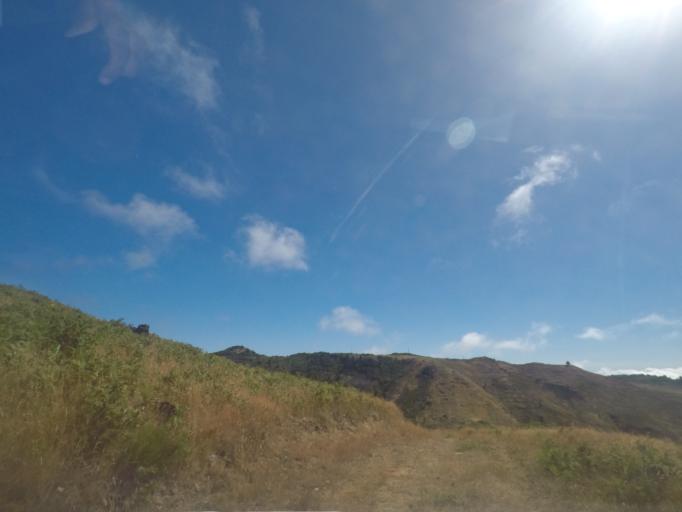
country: PT
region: Madeira
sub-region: Funchal
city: Nossa Senhora do Monte
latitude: 32.7113
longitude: -16.9062
